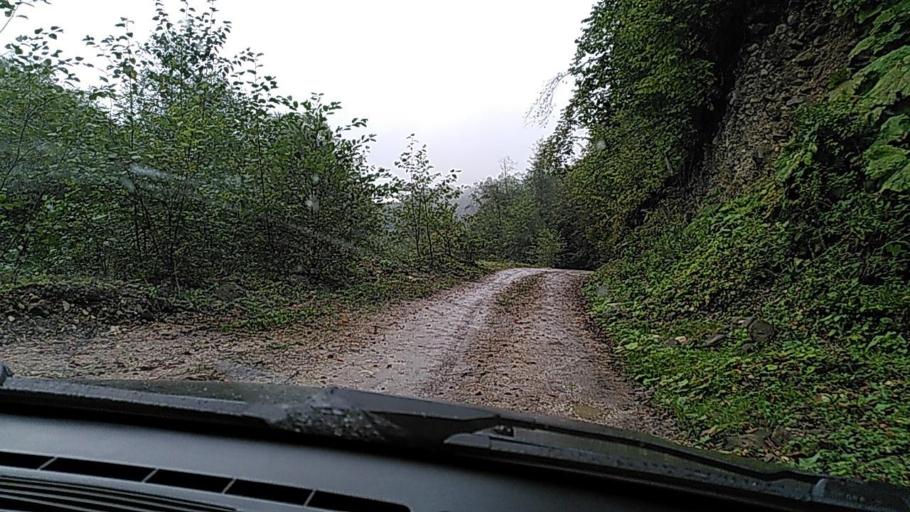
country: RU
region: Kabardino-Balkariya
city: Belaya Rechka
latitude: 43.3996
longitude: 43.4578
